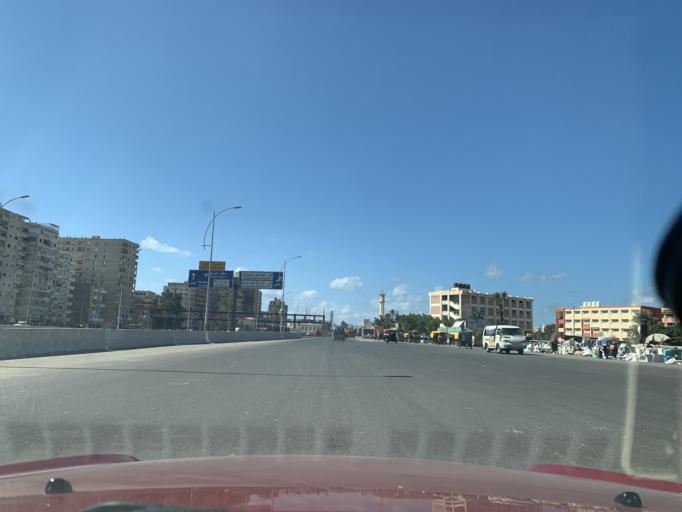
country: EG
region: Alexandria
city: Alexandria
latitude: 31.2194
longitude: 29.9930
